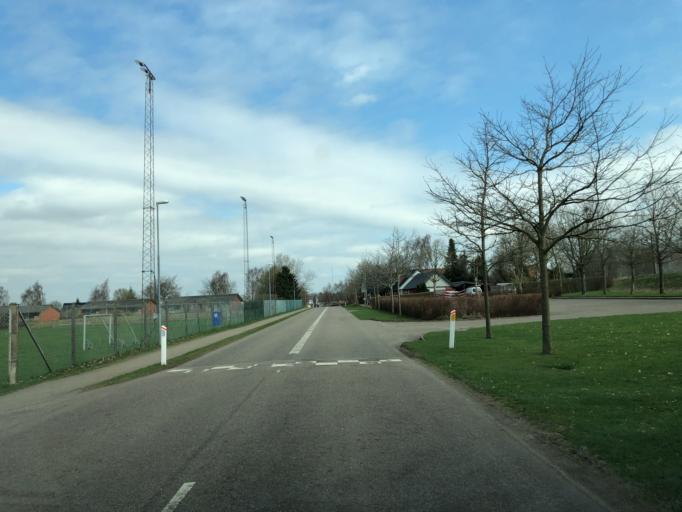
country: DK
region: South Denmark
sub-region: Vejle Kommune
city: Give
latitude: 55.9052
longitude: 9.2645
